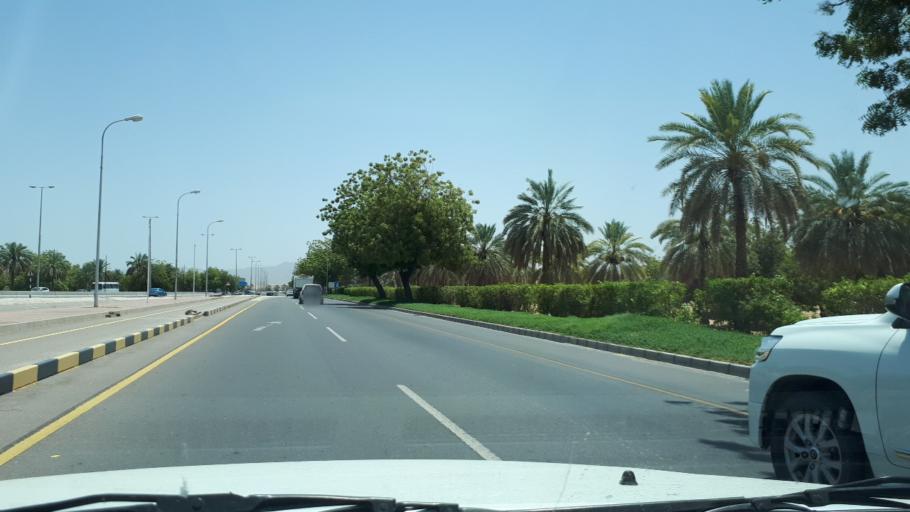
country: OM
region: Muhafazat Masqat
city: As Sib al Jadidah
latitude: 23.5863
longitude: 58.2563
